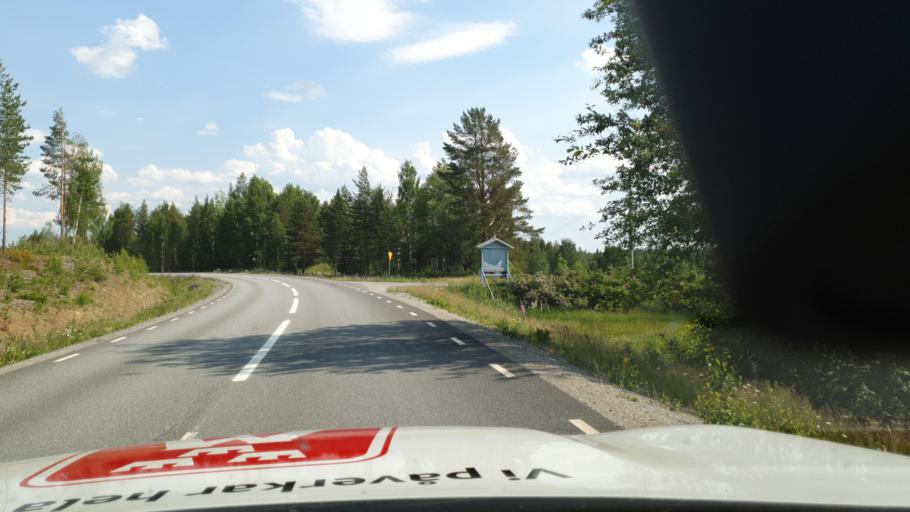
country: SE
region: Vaesterbotten
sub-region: Skelleftea Kommun
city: Boliden
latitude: 64.7409
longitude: 20.3627
